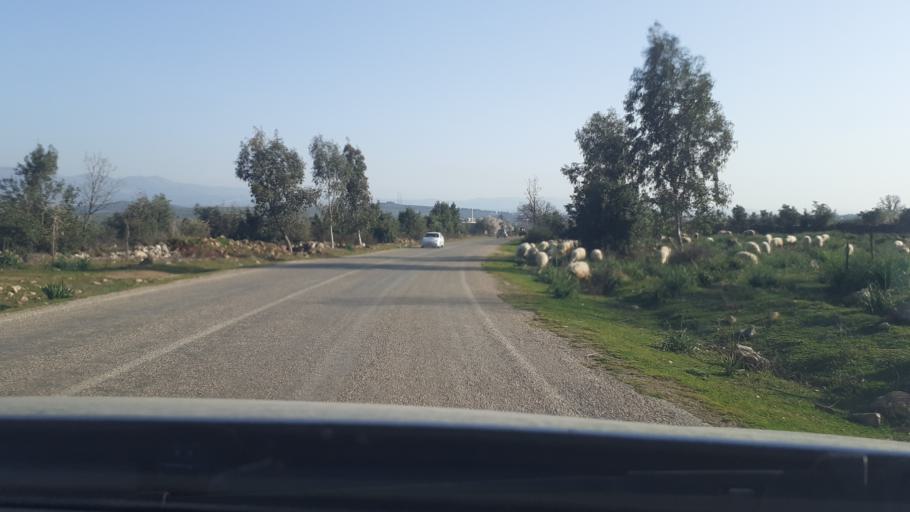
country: TR
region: Hatay
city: Aktepe
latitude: 36.7254
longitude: 36.4848
